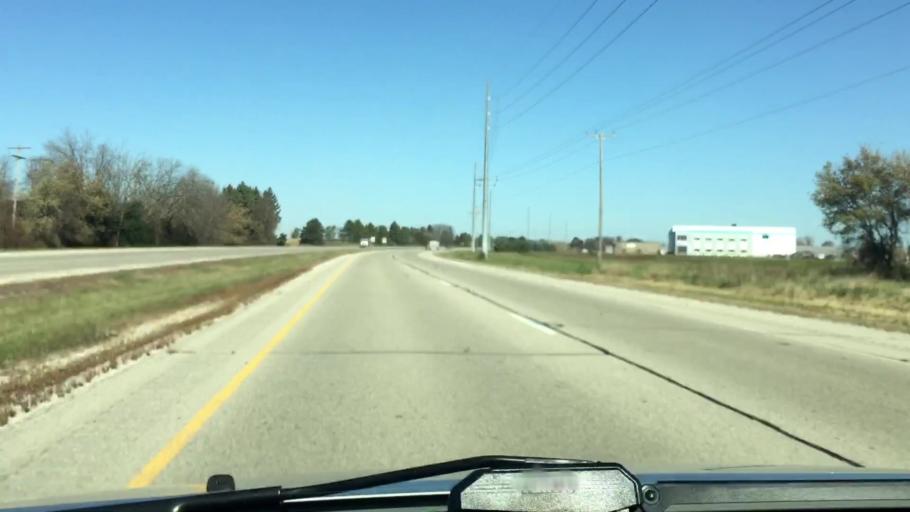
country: US
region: Wisconsin
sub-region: Waukesha County
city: Sussex
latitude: 43.1042
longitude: -88.2094
